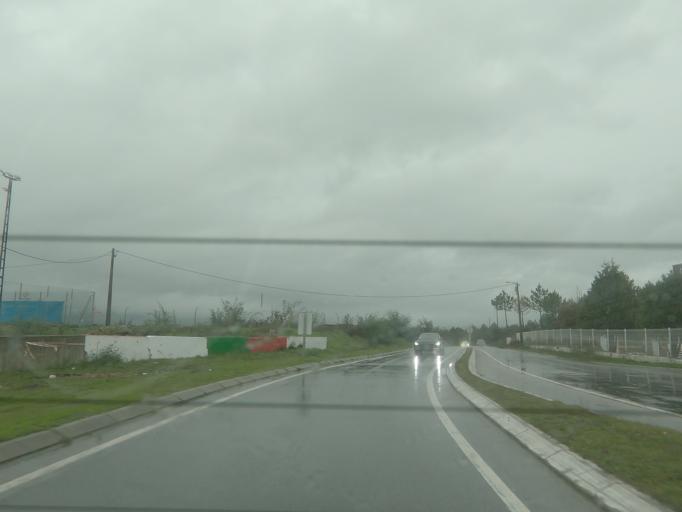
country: PT
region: Vila Real
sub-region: Vila Real
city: Vila Real
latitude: 41.2767
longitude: -7.7177
